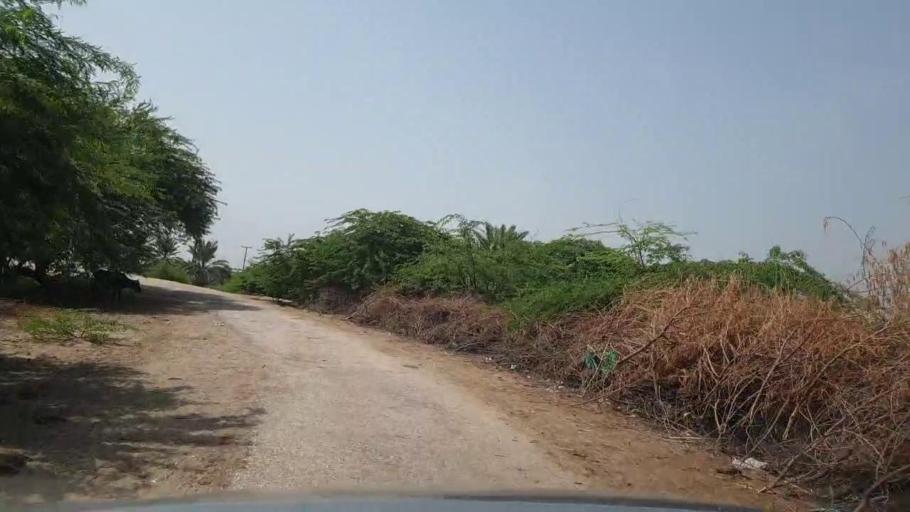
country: PK
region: Sindh
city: Pano Aqil
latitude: 27.6114
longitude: 69.1458
